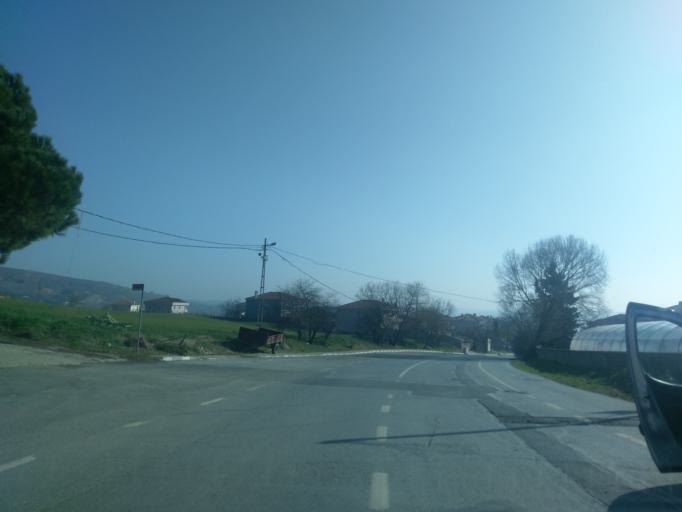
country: TR
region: Istanbul
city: Catalca
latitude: 41.1215
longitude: 28.4509
